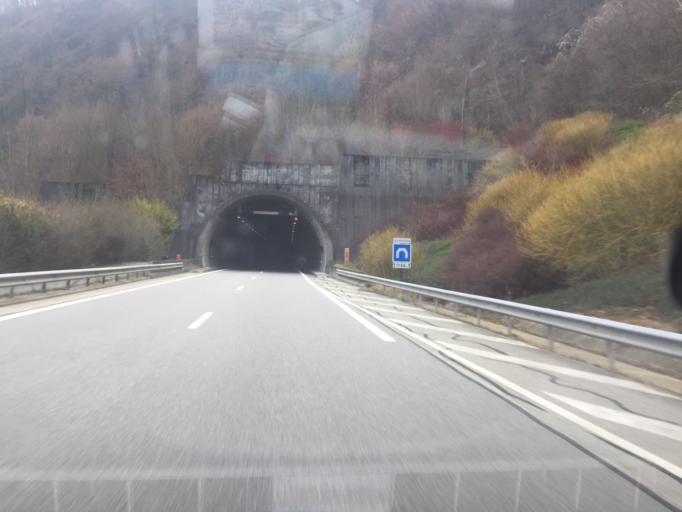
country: FR
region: Rhone-Alpes
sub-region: Departement de la Savoie
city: Aiton
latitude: 45.5196
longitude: 6.3086
